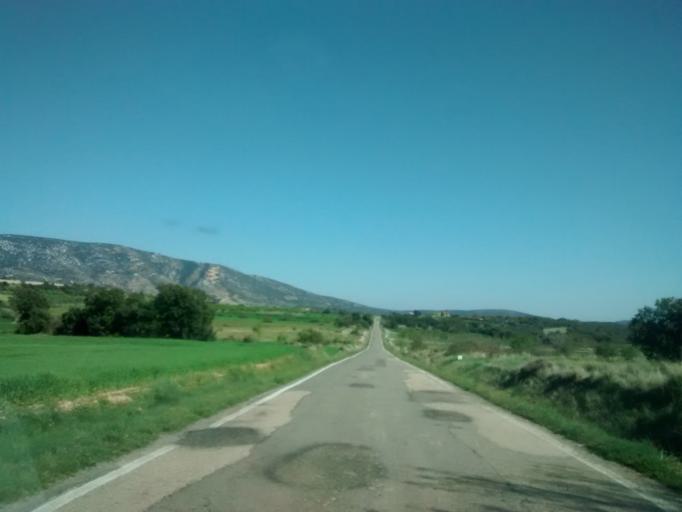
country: ES
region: Aragon
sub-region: Provincia de Huesca
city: Ibieca
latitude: 42.2169
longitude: -0.1826
